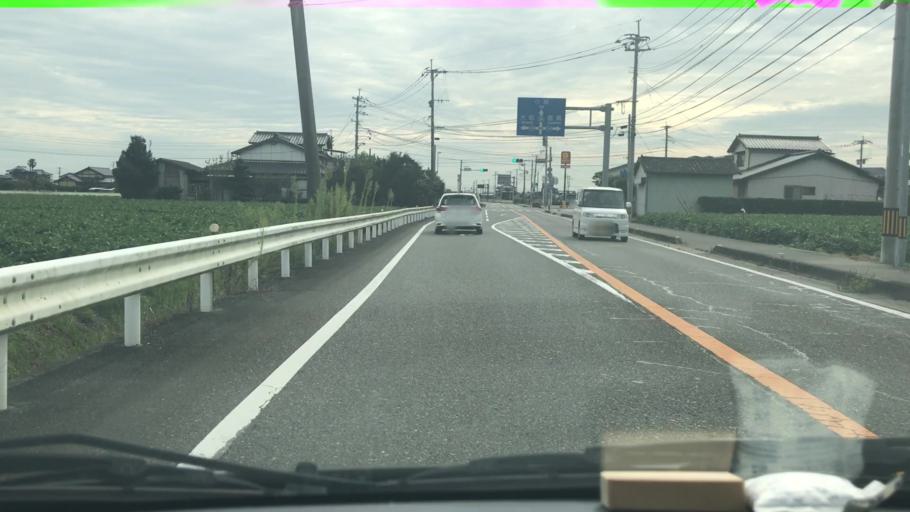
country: JP
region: Saga Prefecture
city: Takeocho-takeo
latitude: 33.1989
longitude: 130.1012
